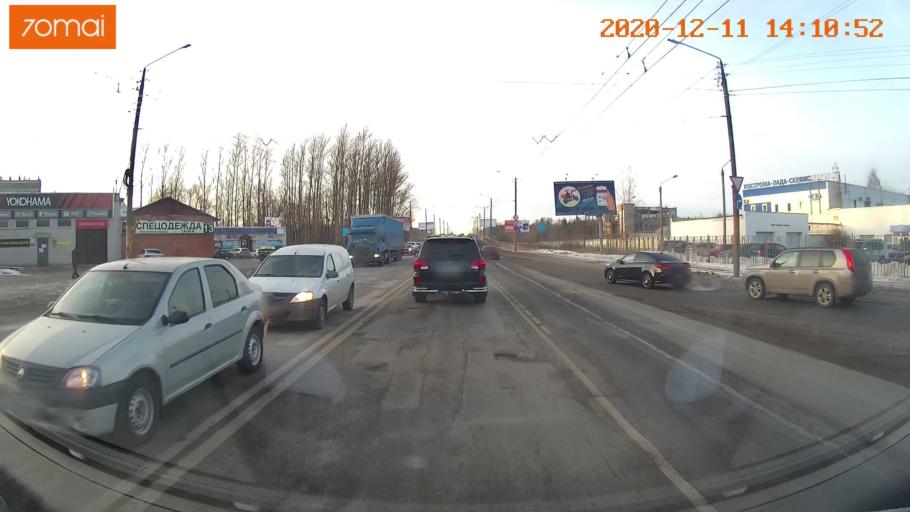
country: RU
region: Kostroma
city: Oktyabr'skiy
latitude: 57.7412
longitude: 40.9765
